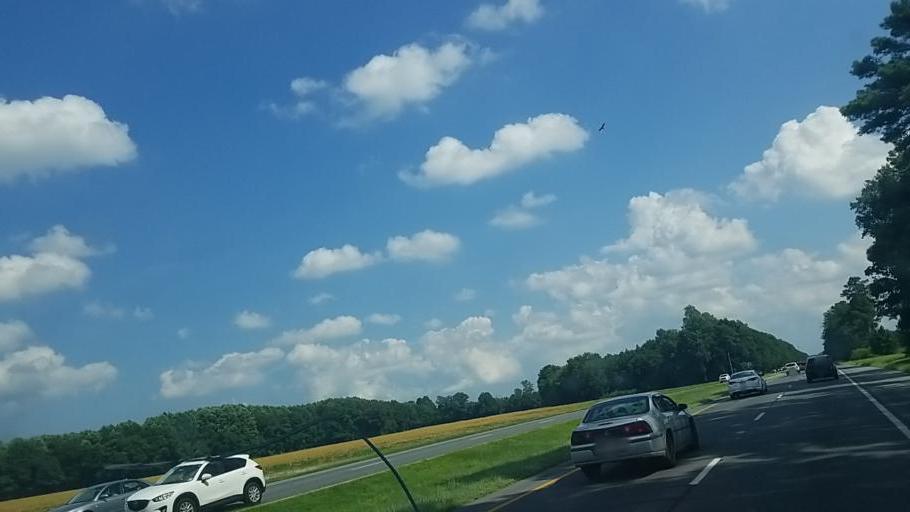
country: US
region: Delaware
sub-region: Sussex County
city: Millsboro
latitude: 38.6125
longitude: -75.3301
